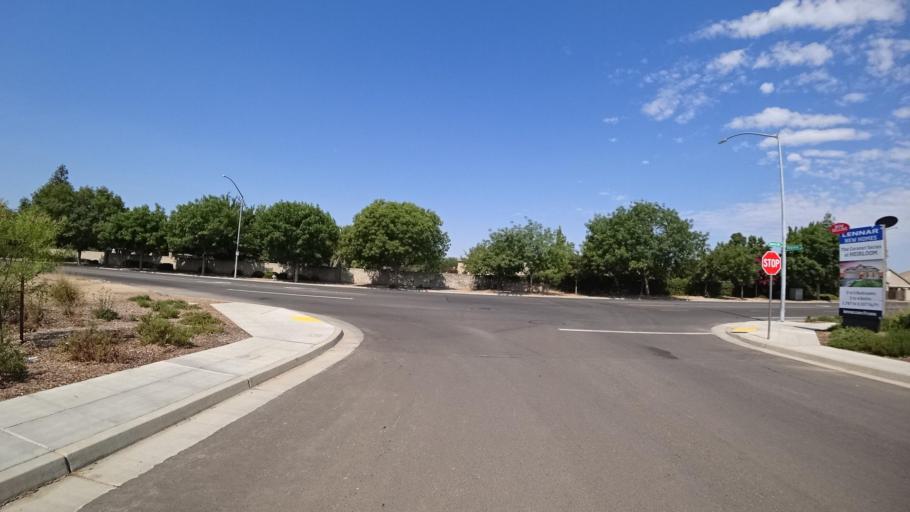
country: US
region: California
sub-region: Fresno County
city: Sunnyside
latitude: 36.7168
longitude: -119.6907
